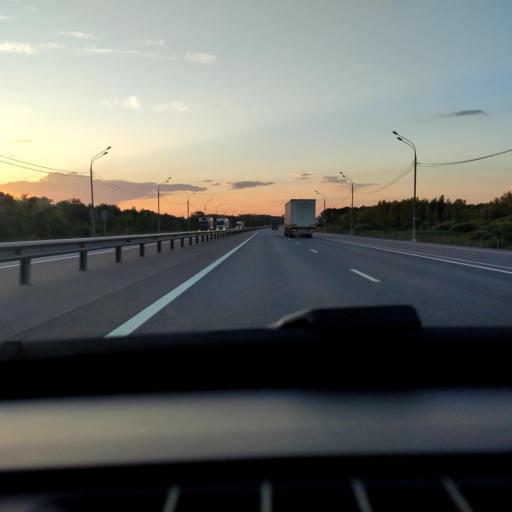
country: RU
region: Lipetsk
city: Khlevnoye
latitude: 52.2637
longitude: 39.0612
